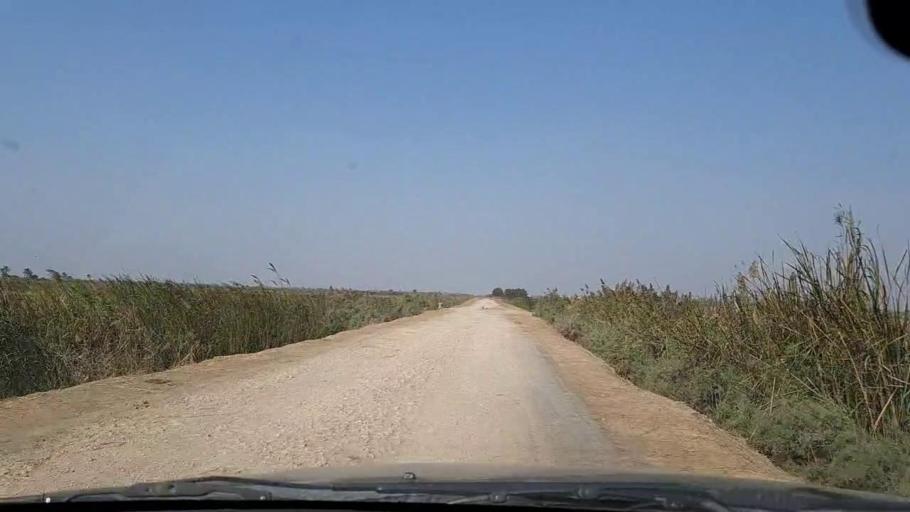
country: PK
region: Sindh
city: Mirpur Sakro
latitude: 24.3559
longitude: 67.6831
